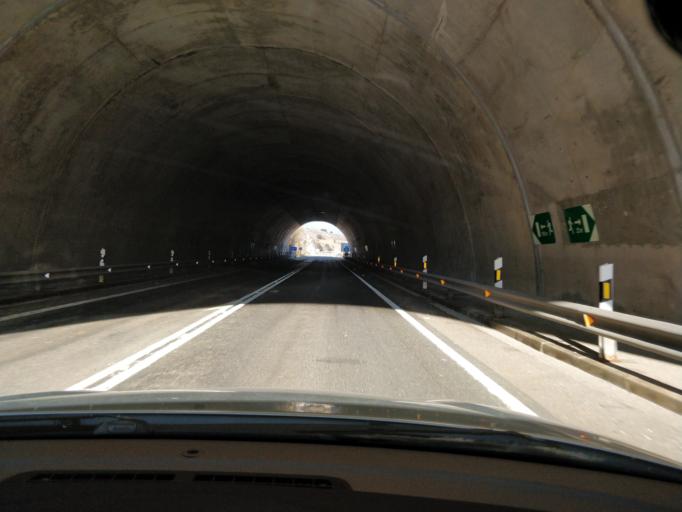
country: ES
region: Castille and Leon
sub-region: Provincia de Burgos
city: Quintanaortuno
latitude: 42.5113
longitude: -3.6960
